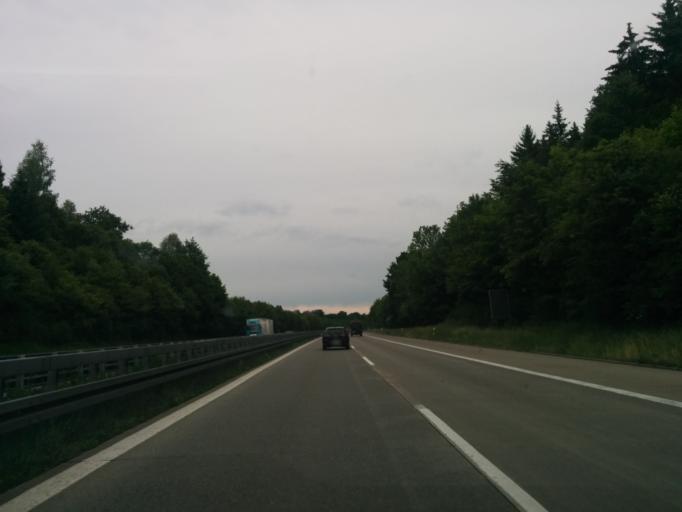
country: DE
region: Baden-Wuerttemberg
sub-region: Tuebingen Region
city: Nerenstetten
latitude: 48.5157
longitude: 10.0813
